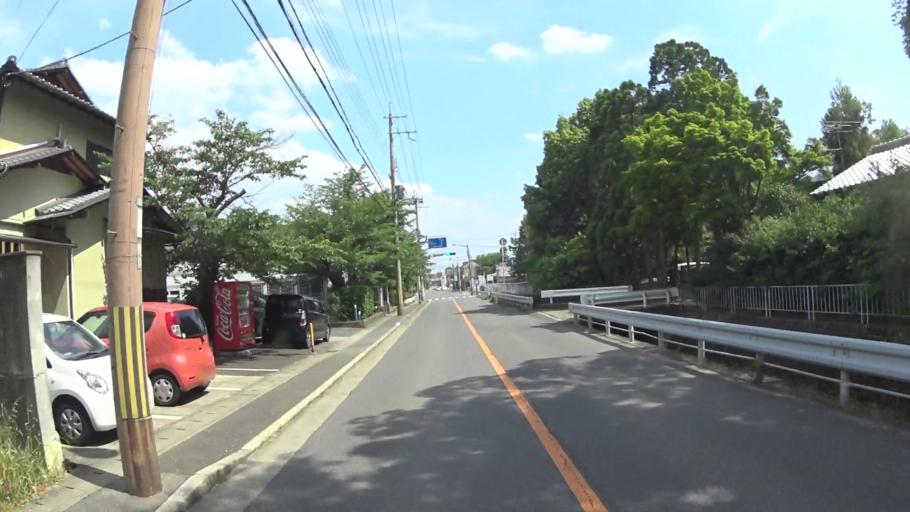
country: JP
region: Kyoto
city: Muko
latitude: 35.0241
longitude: 135.6754
